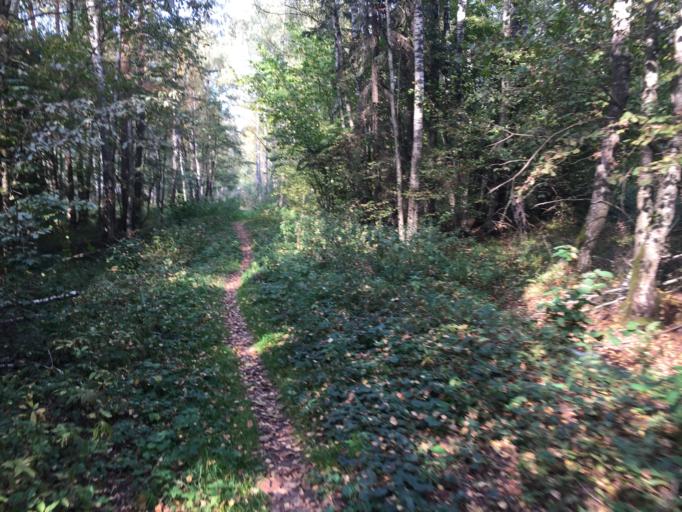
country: RU
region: Moscow
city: Babushkin
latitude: 55.8705
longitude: 37.7420
